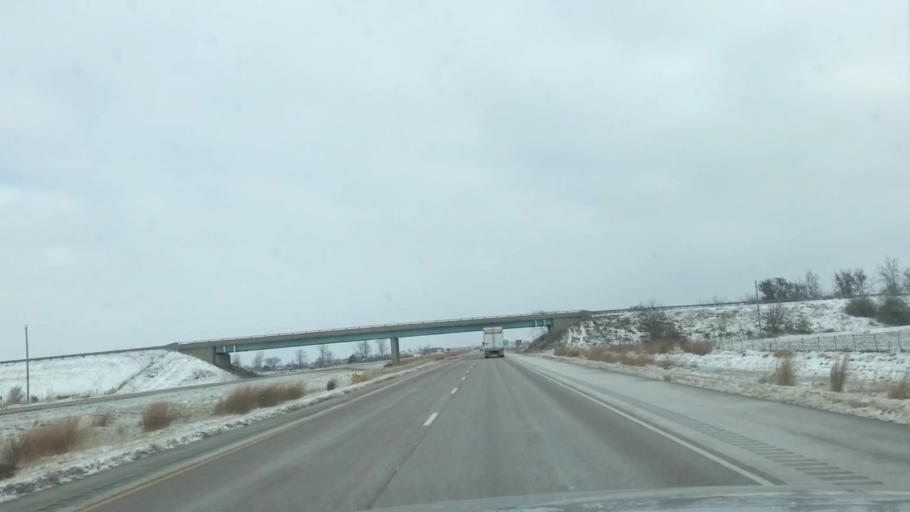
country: US
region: Illinois
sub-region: Montgomery County
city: Litchfield
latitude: 39.1527
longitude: -89.6963
